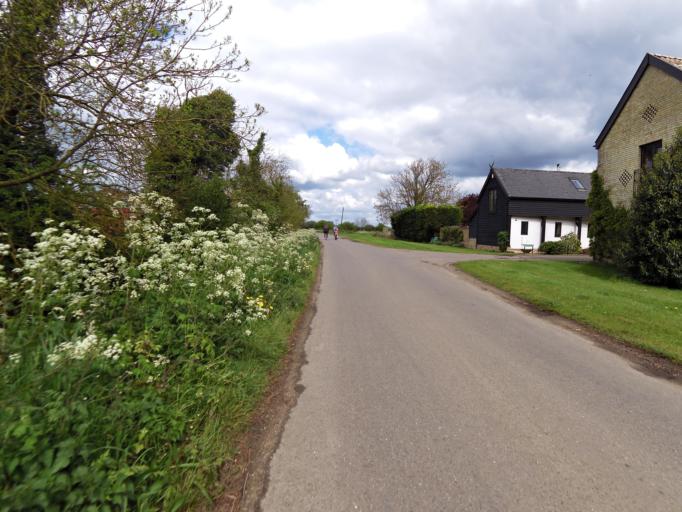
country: GB
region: England
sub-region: Cambridgeshire
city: Bottisham
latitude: 52.2469
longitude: 0.2401
